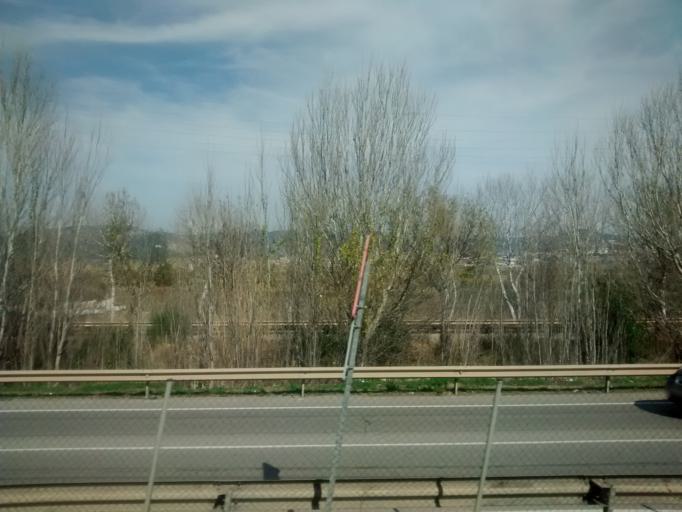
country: ES
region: Catalonia
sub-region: Provincia de Barcelona
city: Santa Coloma de Cervello
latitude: 41.3673
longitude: 2.0280
